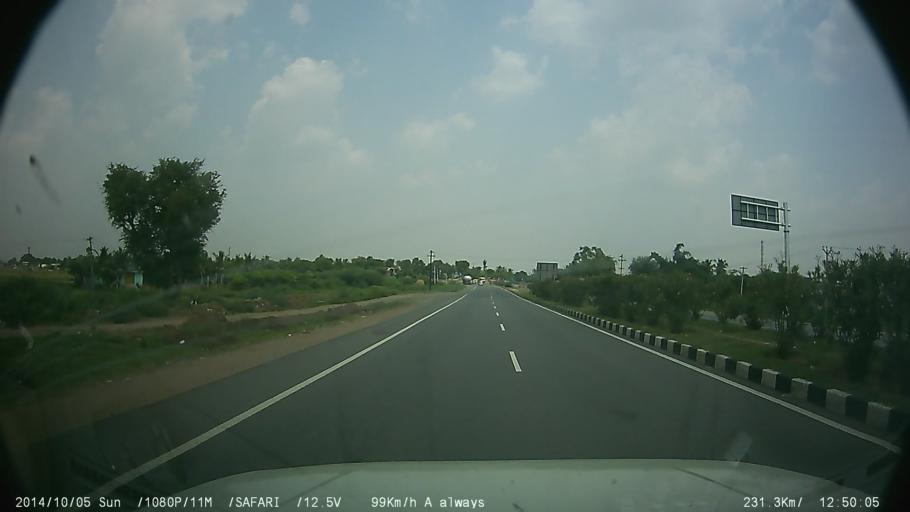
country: IN
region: Tamil Nadu
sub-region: Cuddalore
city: Vriddhachalam
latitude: 11.7129
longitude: 79.3299
